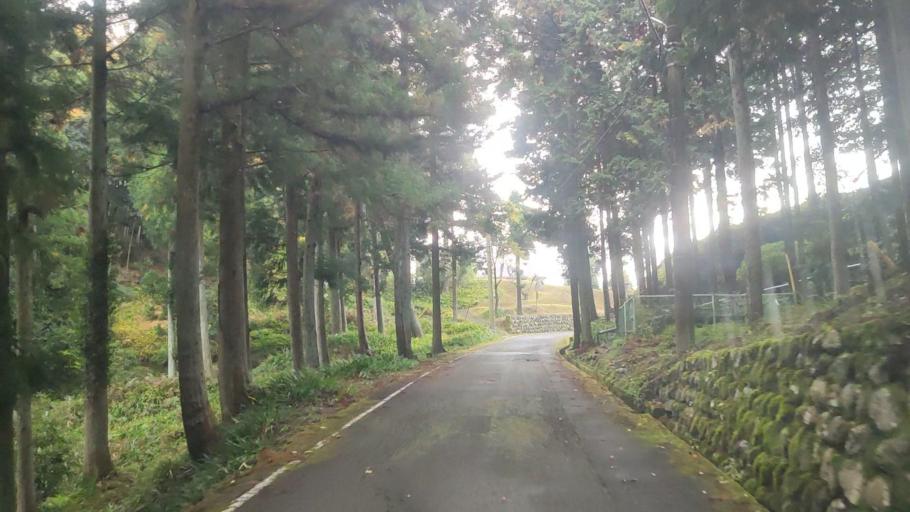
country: JP
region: Shizuoka
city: Fujinomiya
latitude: 35.3196
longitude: 138.4364
